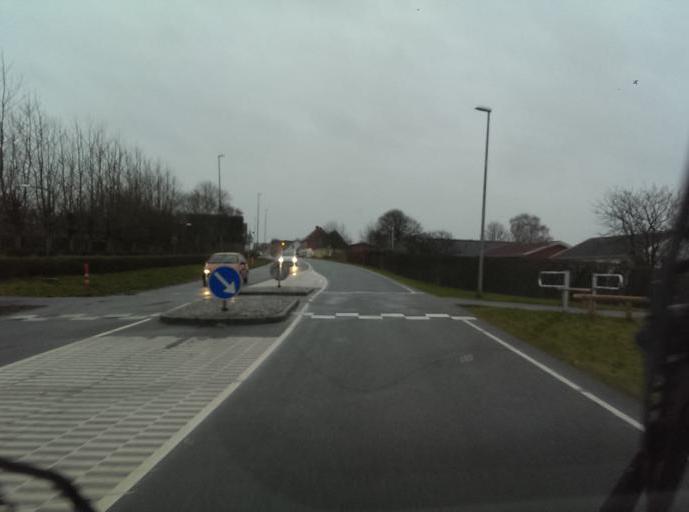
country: DK
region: South Denmark
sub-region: Esbjerg Kommune
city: Tjaereborg
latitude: 55.5030
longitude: 8.5369
